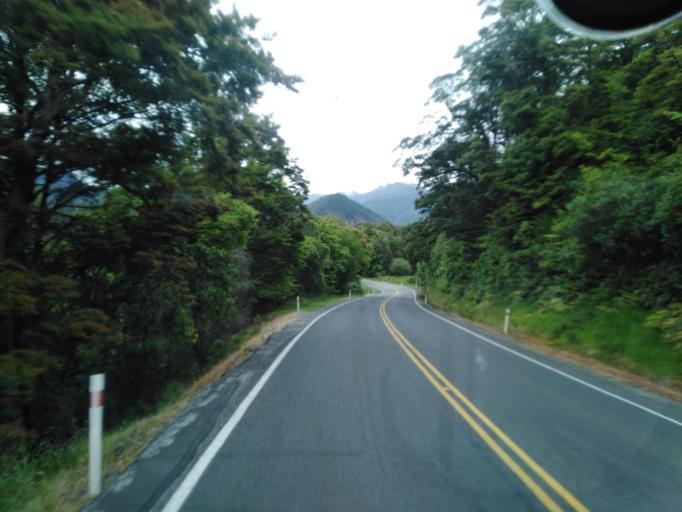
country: NZ
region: Tasman
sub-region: Tasman District
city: Wakefield
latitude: -41.7089
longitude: 172.5812
